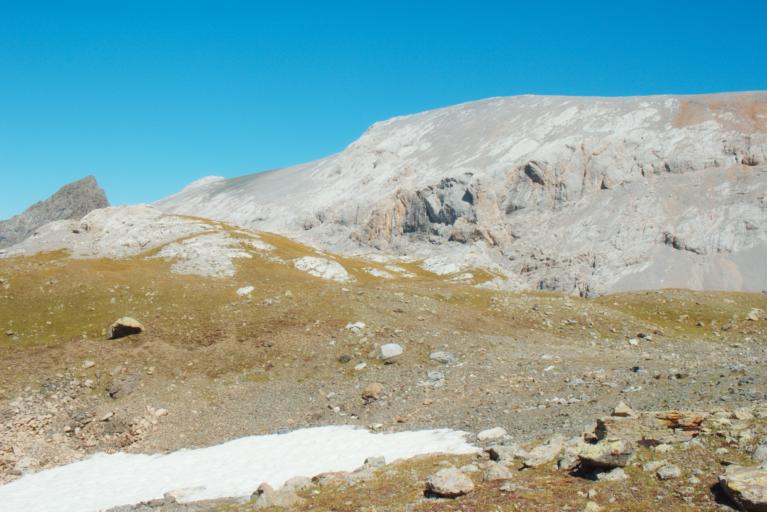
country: RU
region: Karachayevo-Cherkesiya
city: Nizhniy Arkhyz
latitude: 43.5974
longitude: 41.1751
